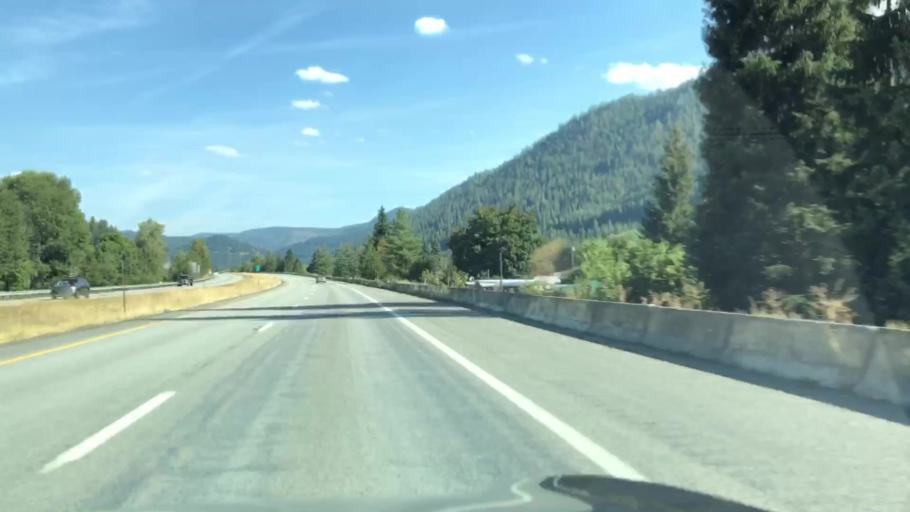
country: US
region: Idaho
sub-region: Shoshone County
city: Osburn
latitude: 47.5158
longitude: -116.0318
